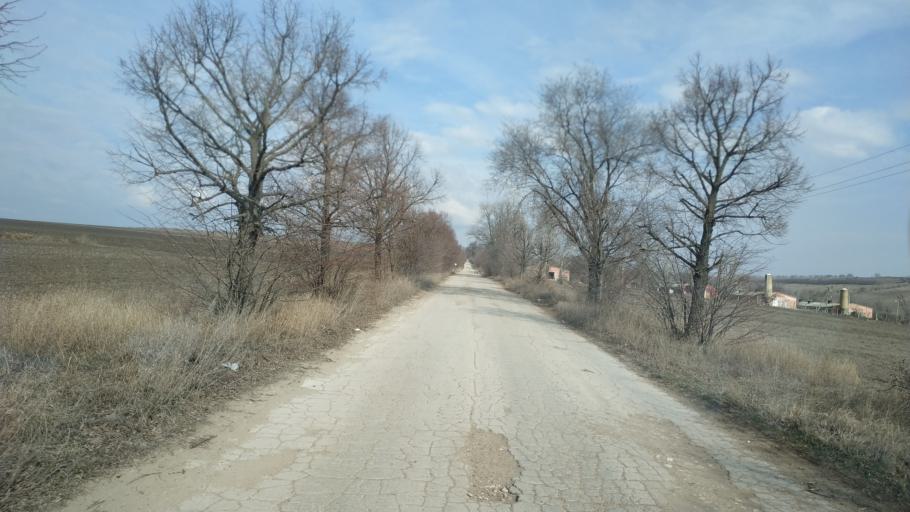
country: MD
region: Anenii Noi
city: Anenii Noi
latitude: 46.9384
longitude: 29.1087
